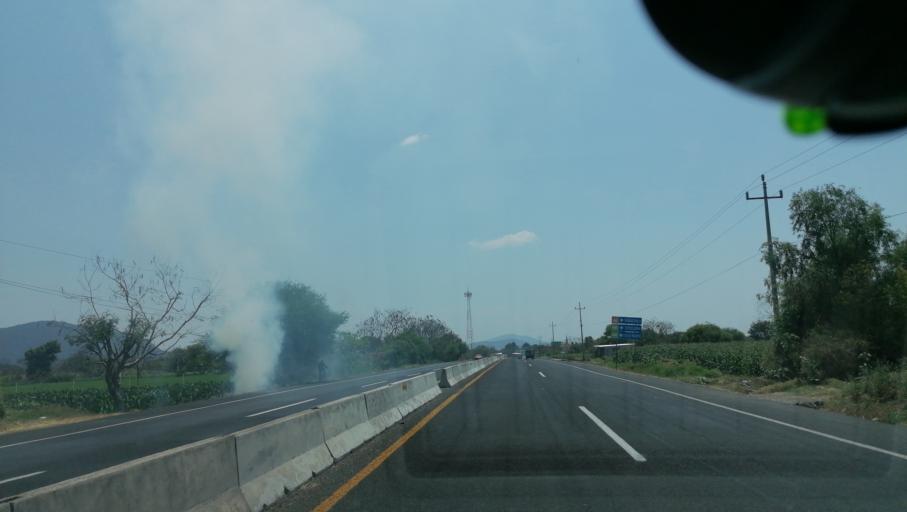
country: MX
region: Puebla
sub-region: Huaquechula
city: Tronconal
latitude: 18.8002
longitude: -98.4505
